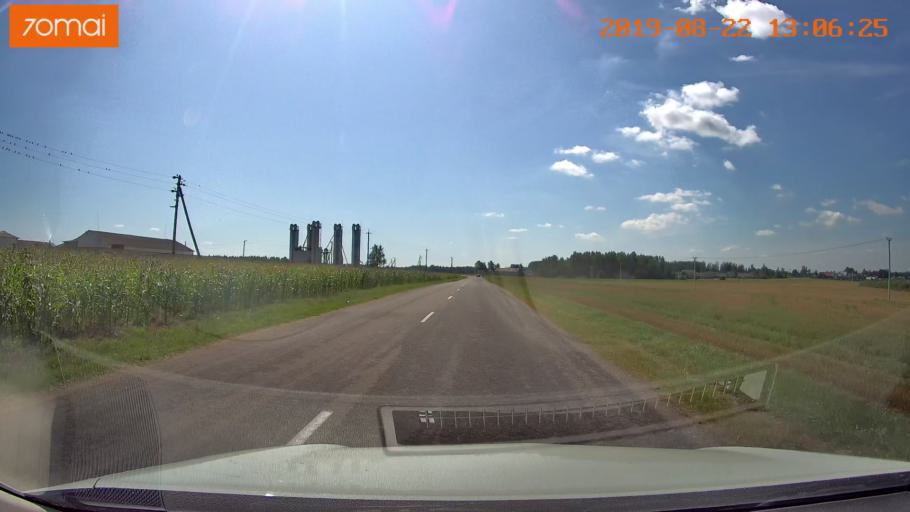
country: BY
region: Minsk
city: Prawdzinski
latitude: 53.3473
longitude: 27.8385
